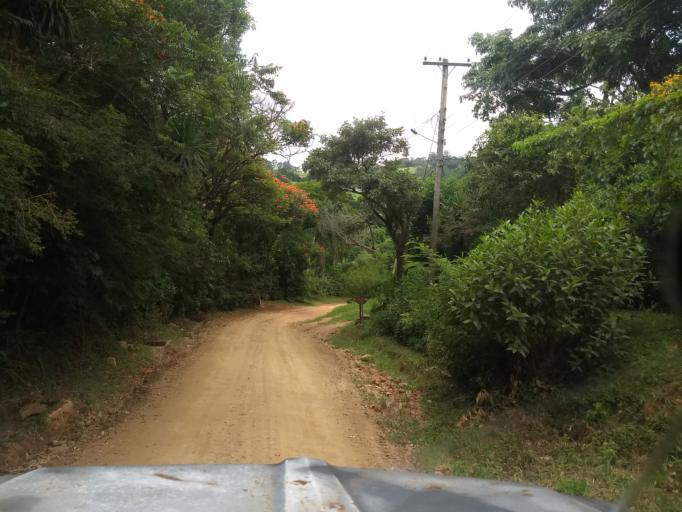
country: BR
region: Sao Paulo
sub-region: Cabreuva
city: Cabreuva
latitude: -23.3880
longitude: -47.1688
